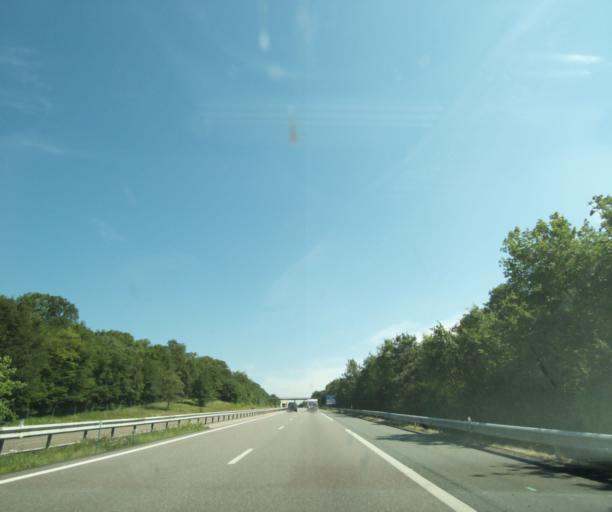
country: FR
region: Lorraine
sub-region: Departement de Meurthe-et-Moselle
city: Colombey-les-Belles
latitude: 48.4994
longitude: 5.9093
